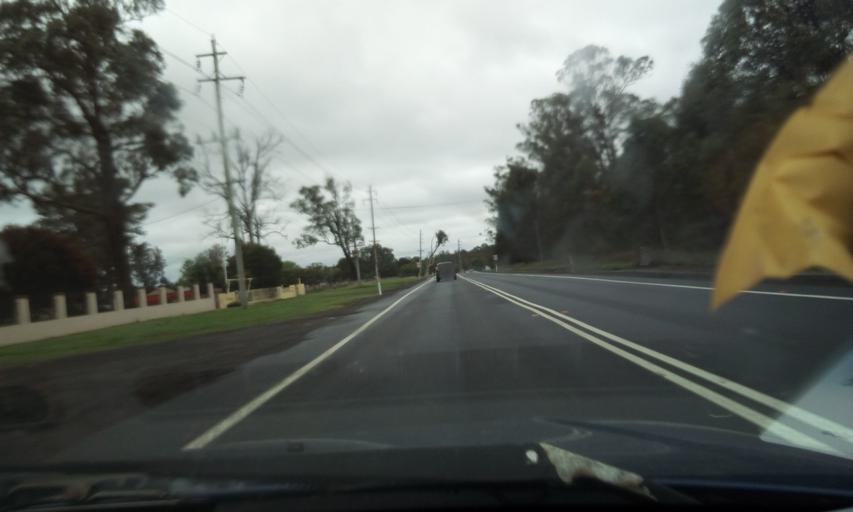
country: AU
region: New South Wales
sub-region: Hawkesbury
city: South Windsor
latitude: -33.6616
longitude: 150.7624
